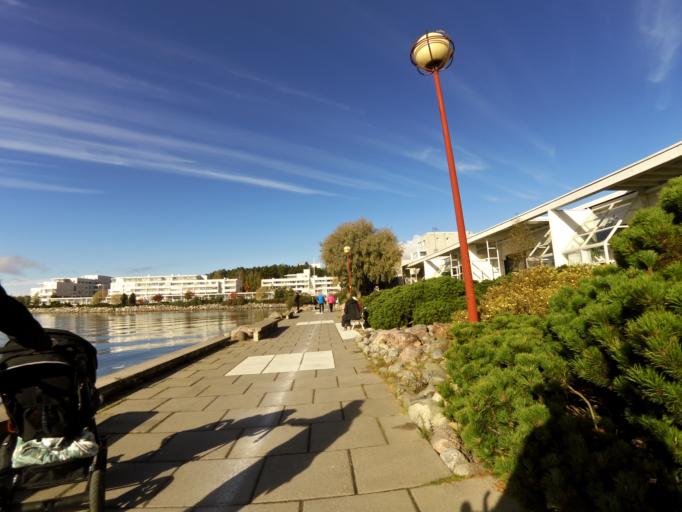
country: FI
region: Uusimaa
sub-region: Helsinki
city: Espoo
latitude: 60.1513
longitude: 24.6333
